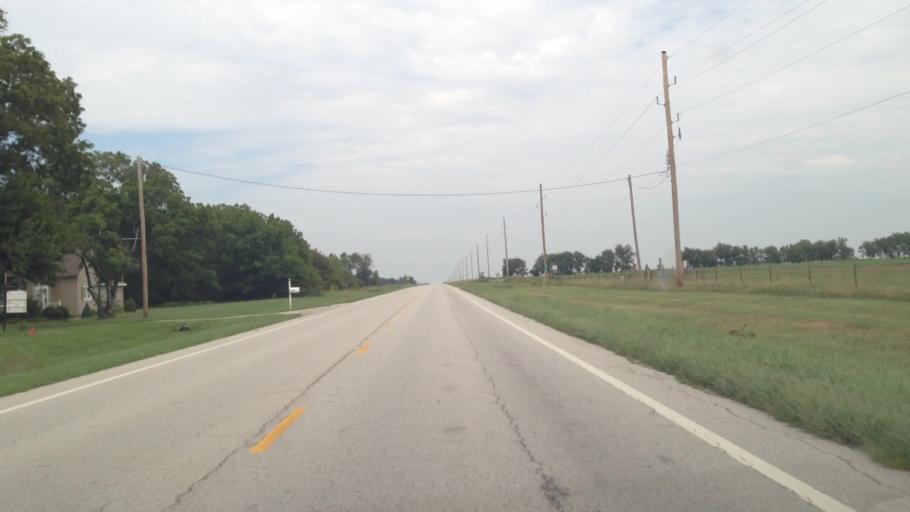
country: US
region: Kansas
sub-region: Allen County
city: Iola
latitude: 37.9691
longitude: -95.1702
